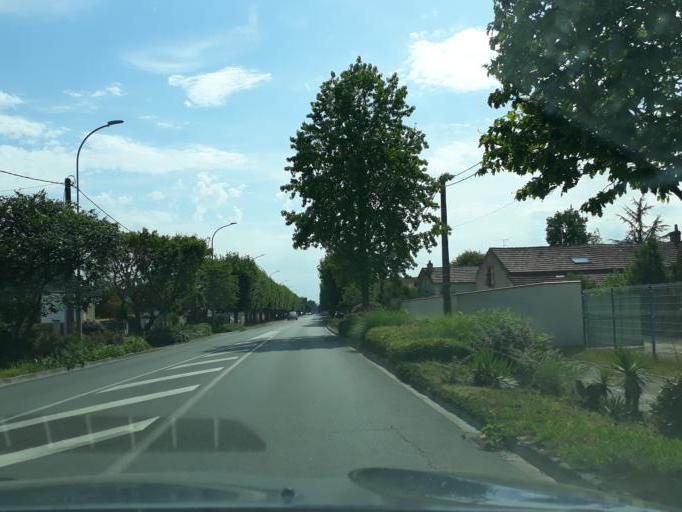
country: FR
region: Centre
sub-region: Departement du Loiret
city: Chateauneuf-sur-Loire
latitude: 47.8729
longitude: 2.2267
